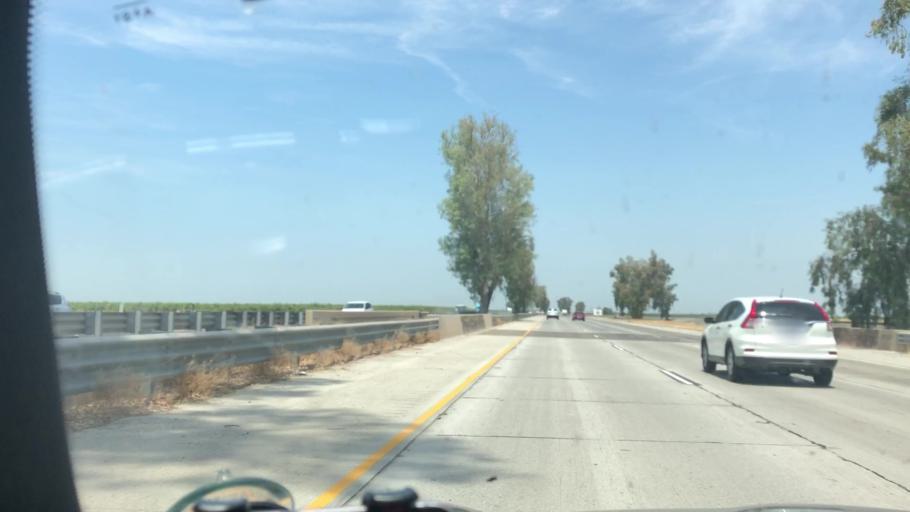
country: US
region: California
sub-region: Tulare County
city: Goshen
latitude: 36.4041
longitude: -119.4562
